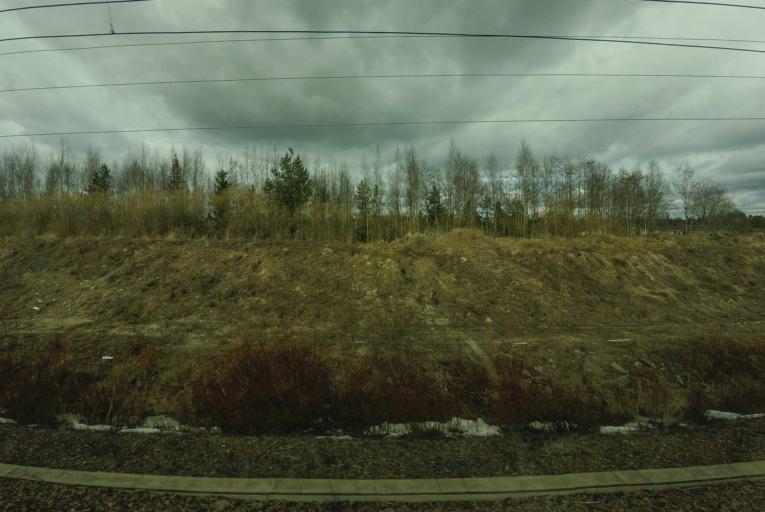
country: FI
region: Kymenlaakso
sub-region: Kouvola
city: Iitti
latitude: 60.8838
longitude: 26.3423
